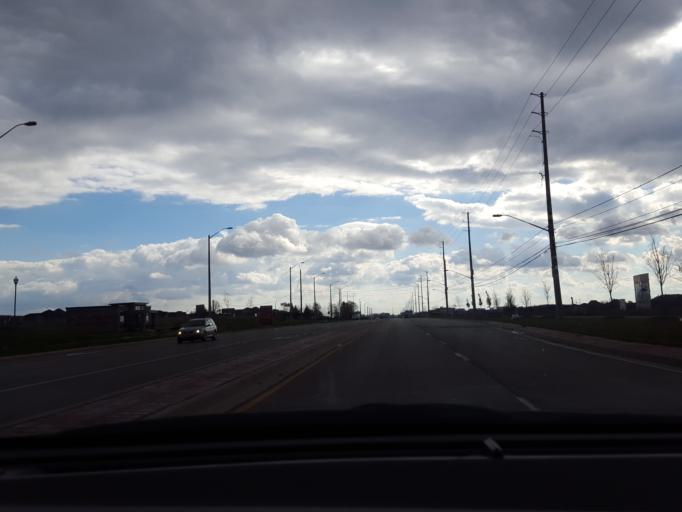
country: CA
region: Ontario
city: Brampton
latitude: 43.6376
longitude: -79.7898
